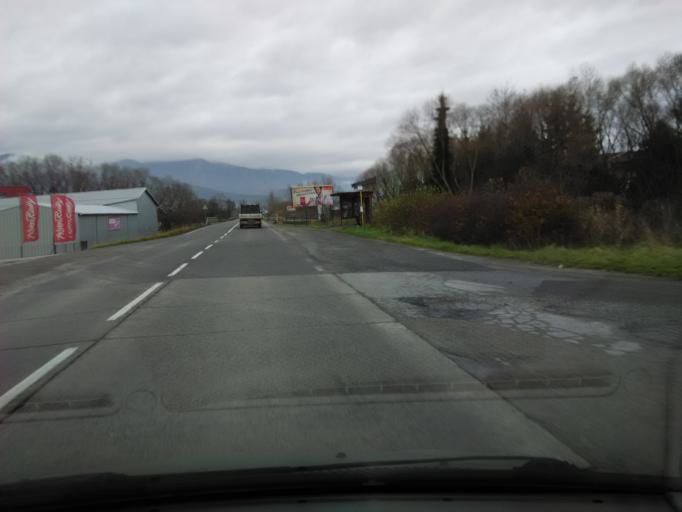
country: SK
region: Zilinsky
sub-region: Okres Martin
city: Martin
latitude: 48.9925
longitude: 18.8913
